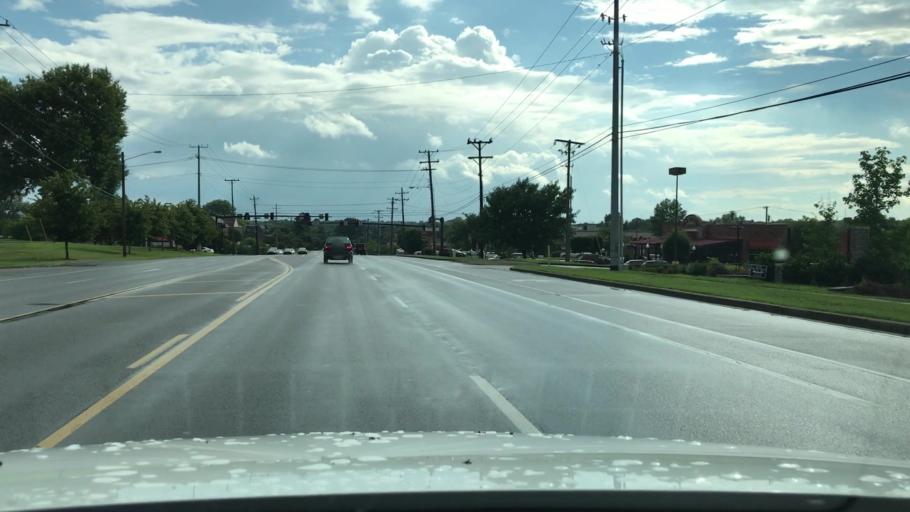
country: US
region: Tennessee
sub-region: Sumner County
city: Hendersonville
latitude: 36.3088
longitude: -86.6037
